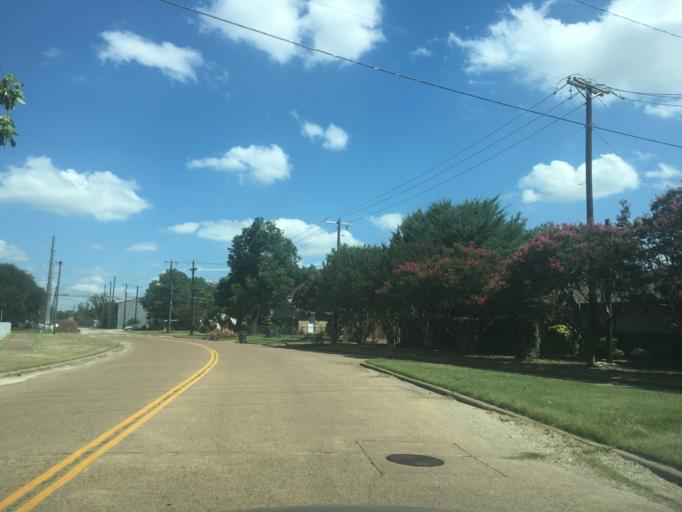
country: US
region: Texas
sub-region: Dallas County
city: Garland
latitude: 32.8367
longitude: -96.6927
